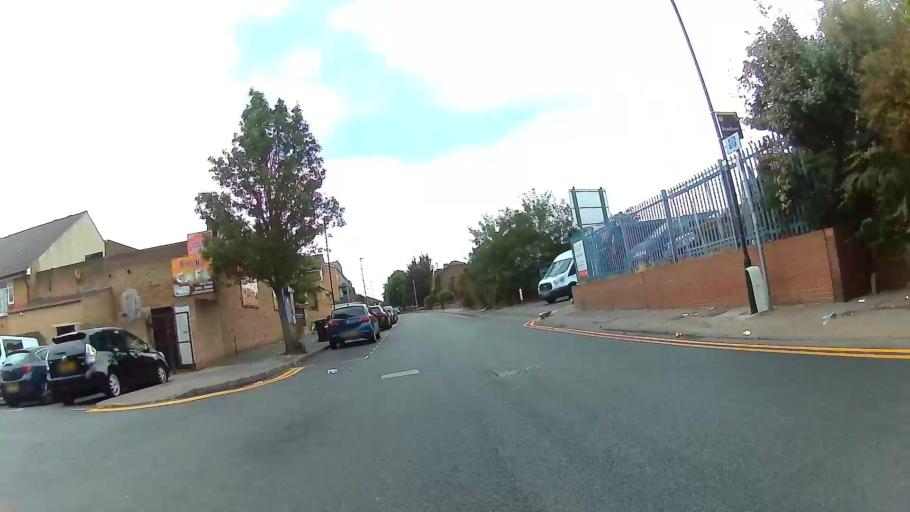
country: GB
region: England
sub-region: Greater London
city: Harringay
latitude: 51.6082
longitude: -0.0755
